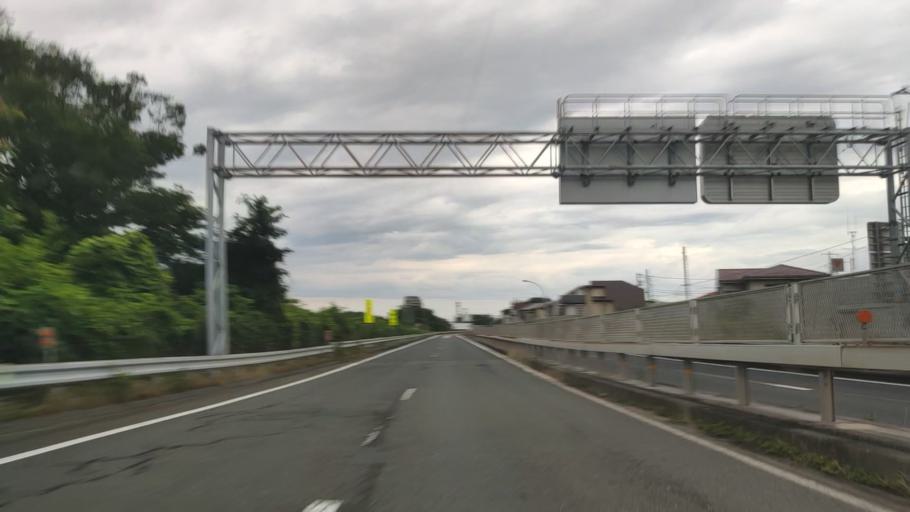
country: JP
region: Kanagawa
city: Odawara
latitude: 35.2458
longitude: 139.1359
